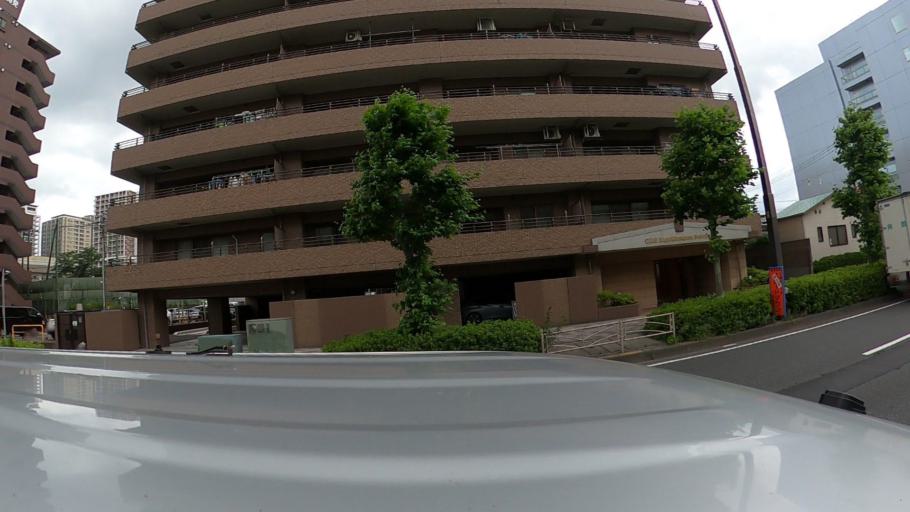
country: JP
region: Kanagawa
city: Yokohama
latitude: 35.4781
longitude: 139.6372
